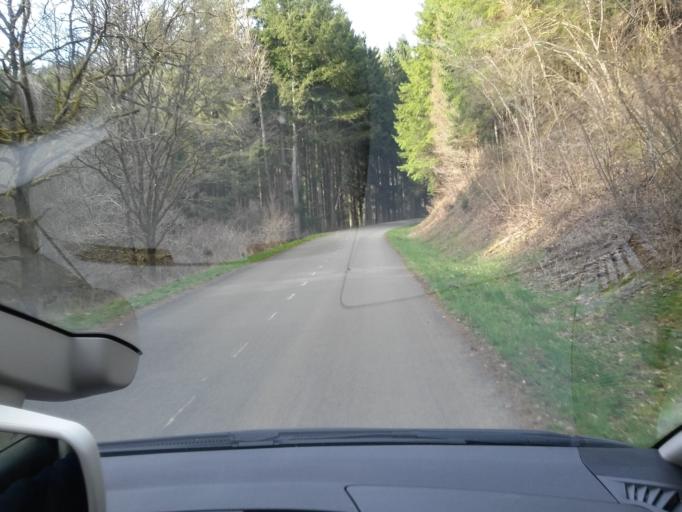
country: BE
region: Wallonia
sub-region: Province du Luxembourg
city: Daverdisse
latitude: 49.9958
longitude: 5.1531
